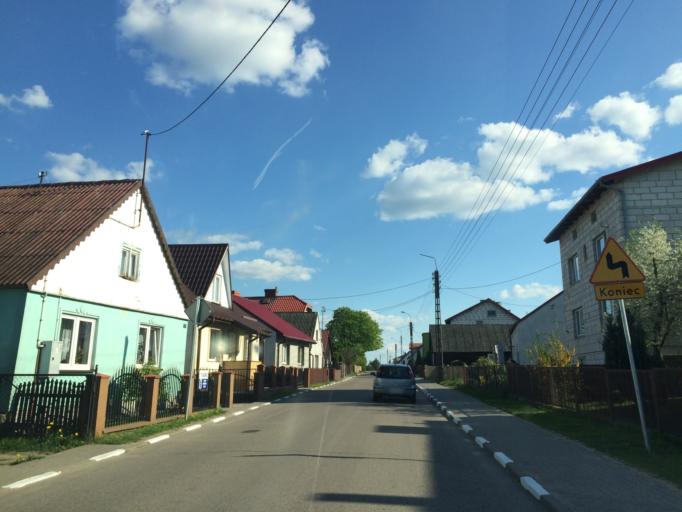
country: PL
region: Warmian-Masurian Voivodeship
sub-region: Powiat dzialdowski
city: Lidzbark
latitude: 53.3006
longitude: 19.8607
